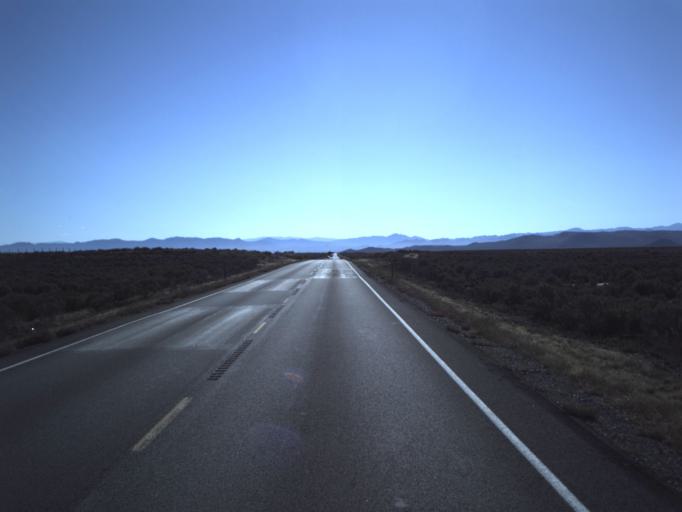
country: US
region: Utah
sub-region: Washington County
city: Enterprise
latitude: 37.7767
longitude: -113.8474
